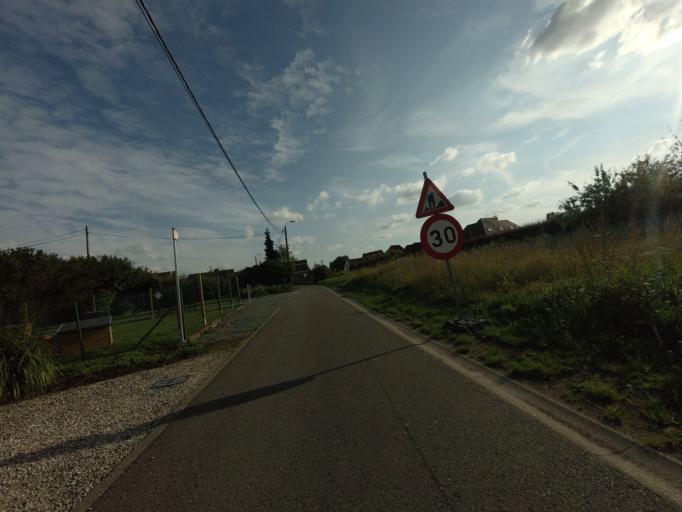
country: BE
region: Flanders
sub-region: Provincie Vlaams-Brabant
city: Kapelle-op-den-Bos
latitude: 51.0167
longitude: 4.3390
